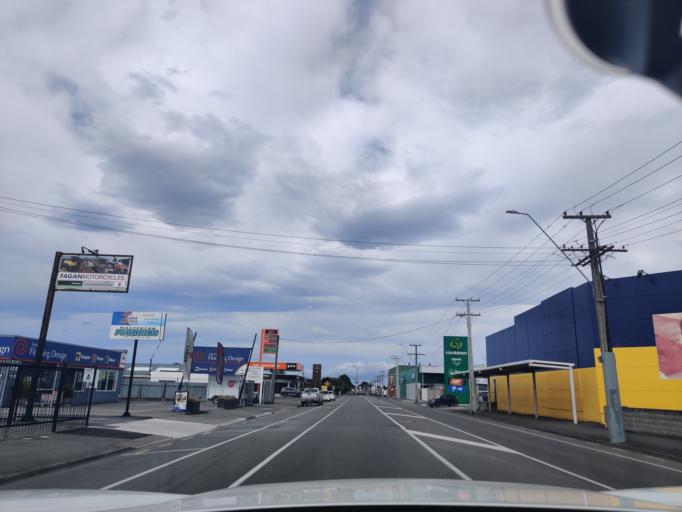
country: NZ
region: Wellington
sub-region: Masterton District
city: Masterton
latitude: -40.9520
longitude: 175.6603
